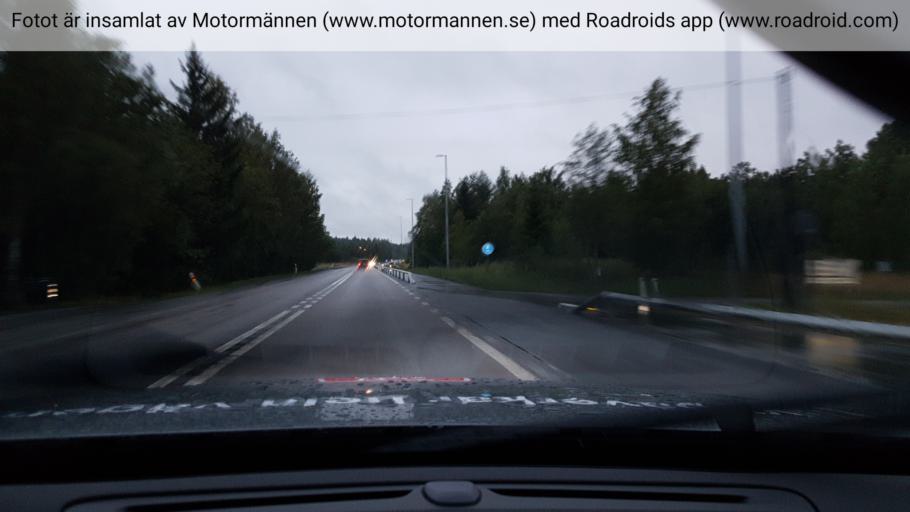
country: SE
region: OErebro
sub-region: Degerfors Kommun
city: Degerfors
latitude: 59.2596
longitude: 14.4410
